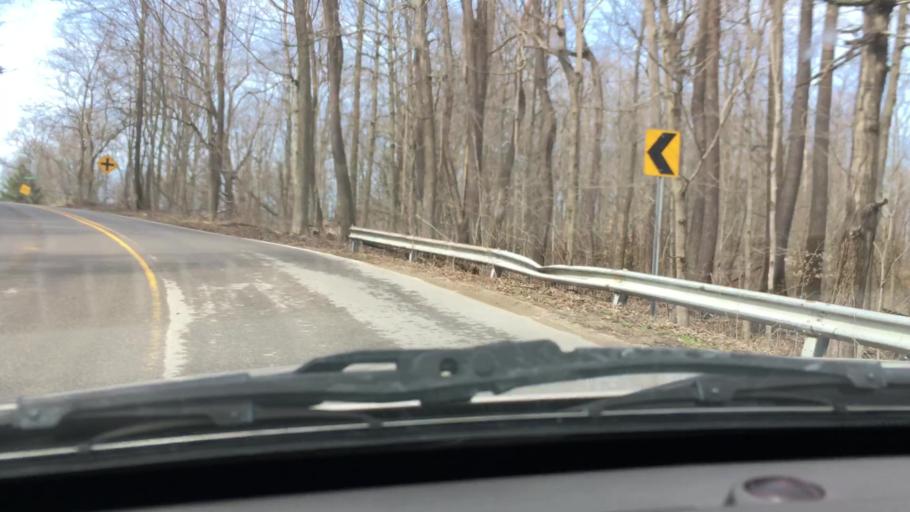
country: US
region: Indiana
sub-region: Morgan County
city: Martinsville
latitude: 39.4784
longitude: -86.4076
